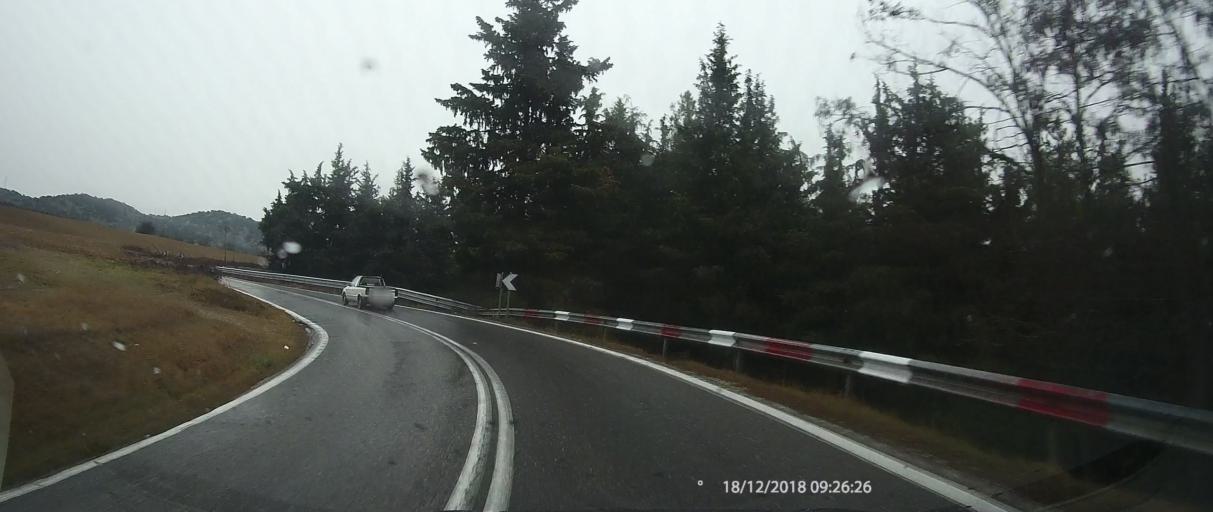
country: GR
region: Thessaly
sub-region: Nomos Larisis
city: Elassona
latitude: 39.9139
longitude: 22.1830
